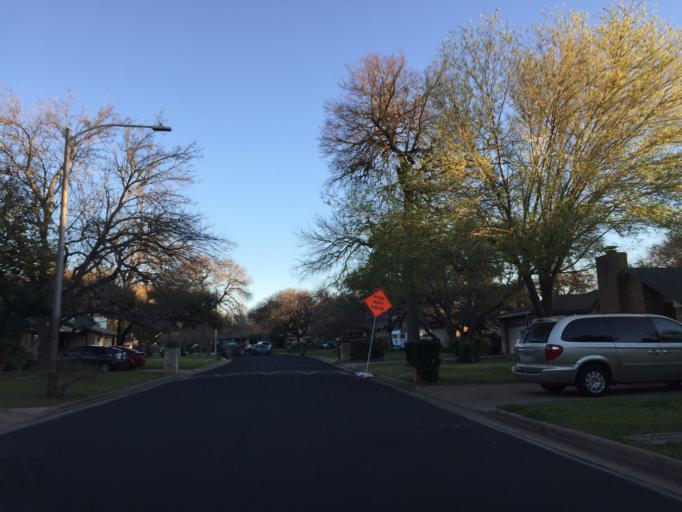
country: US
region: Texas
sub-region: Williamson County
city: Jollyville
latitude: 30.4310
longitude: -97.7760
